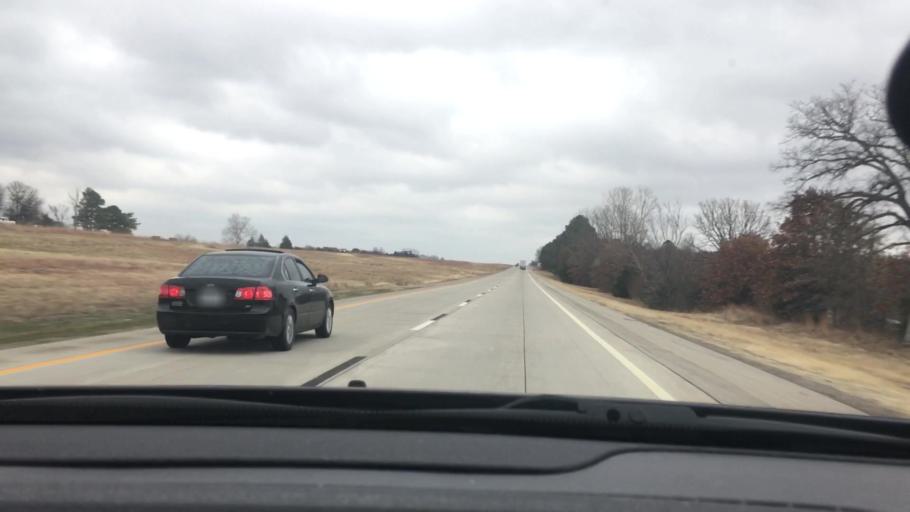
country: US
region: Oklahoma
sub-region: Atoka County
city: Atoka
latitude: 34.1876
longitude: -96.2442
